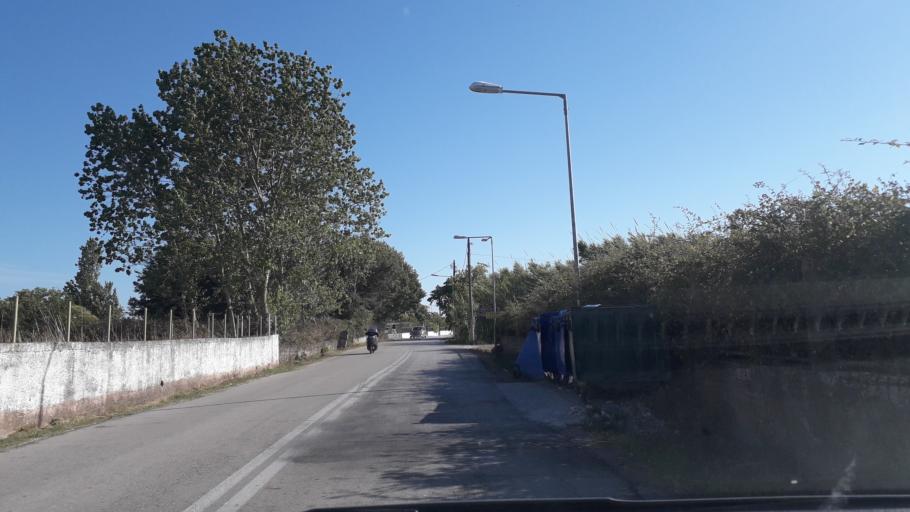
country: GR
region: Ionian Islands
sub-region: Nomos Kerkyras
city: Perivoli
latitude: 39.4317
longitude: 19.9524
